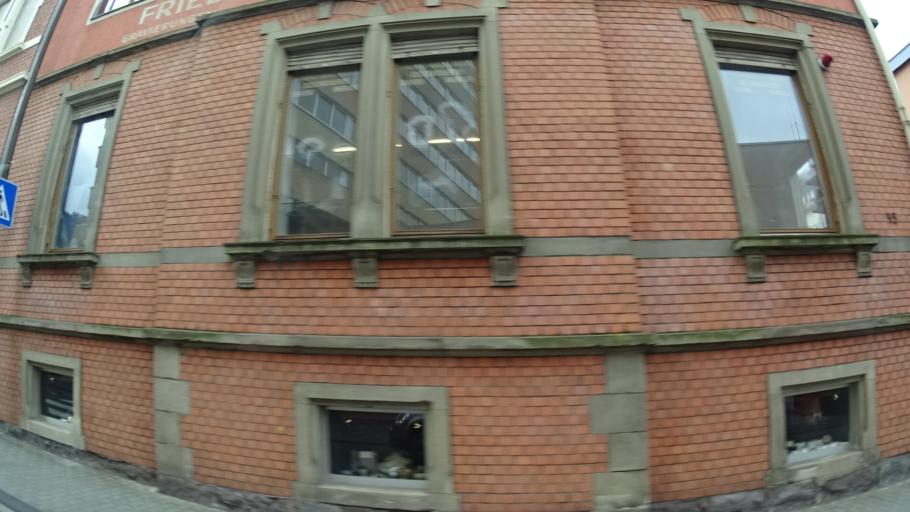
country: DE
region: Rheinland-Pfalz
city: Idar-Oberstein
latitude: 49.7192
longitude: 7.3019
